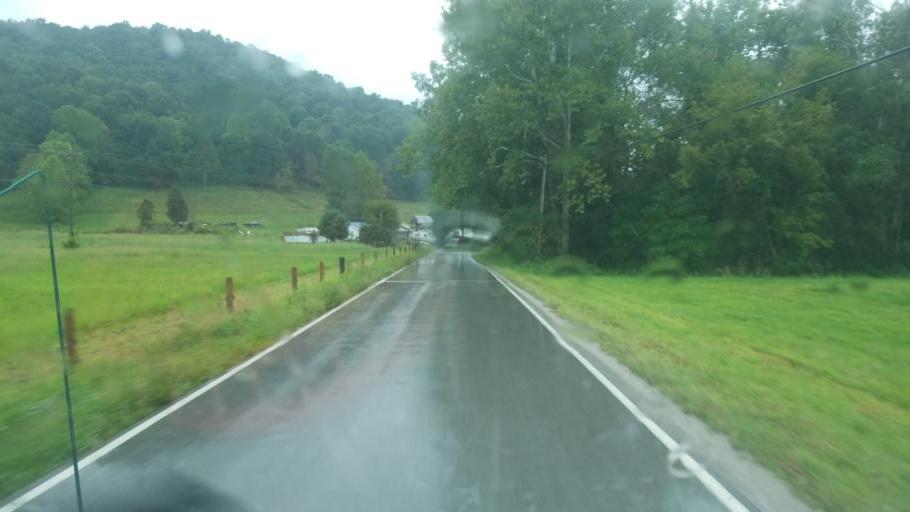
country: US
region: Kentucky
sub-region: Lewis County
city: Vanceburg
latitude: 38.5688
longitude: -83.4329
